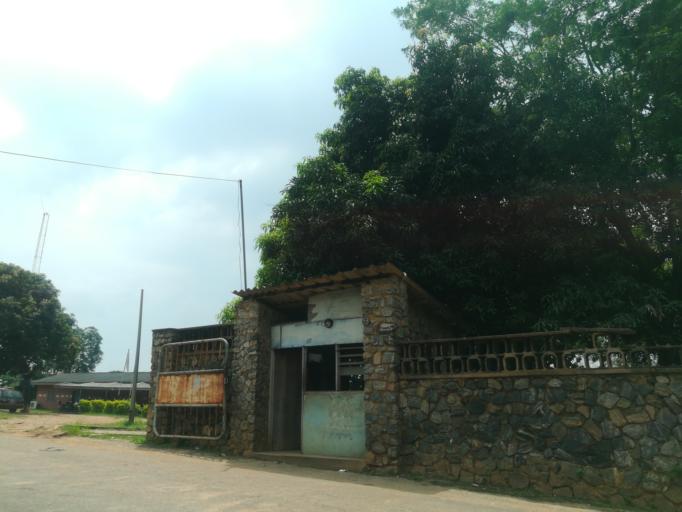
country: NG
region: Oyo
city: Ibadan
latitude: 7.4097
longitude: 3.9057
